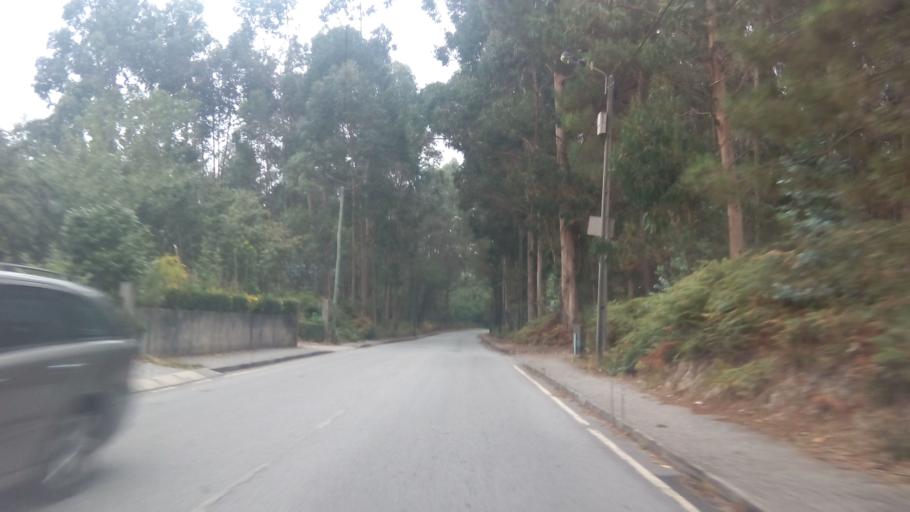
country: PT
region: Porto
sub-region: Paredes
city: Rebordosa
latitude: 41.2176
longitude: -8.3778
